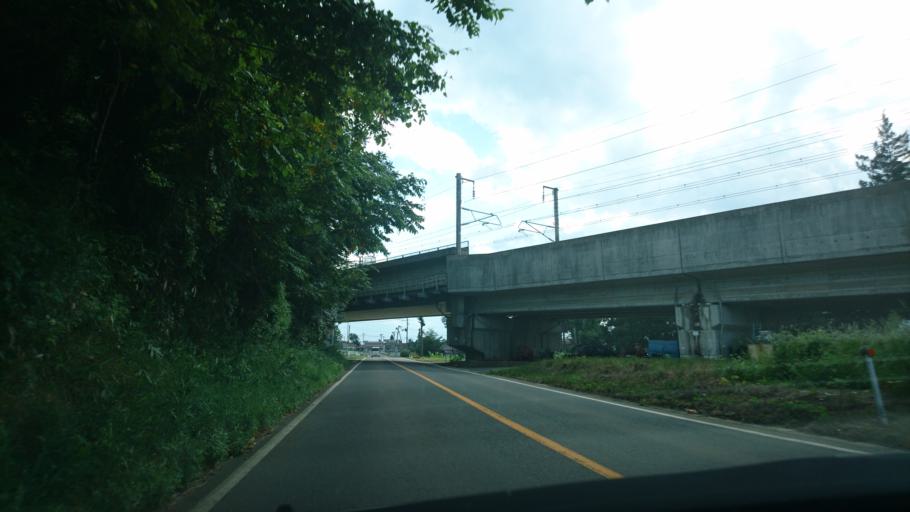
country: JP
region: Iwate
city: Hanamaki
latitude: 39.5070
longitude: 141.1734
